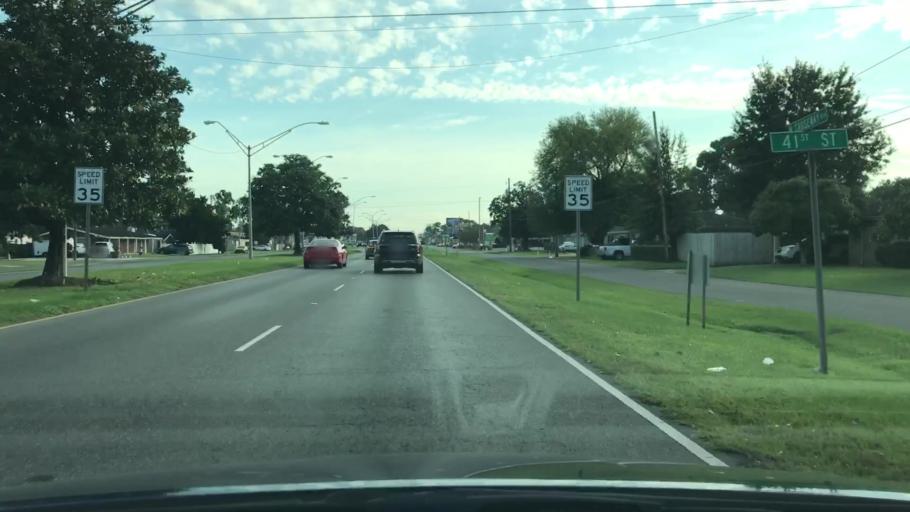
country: US
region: Louisiana
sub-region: Jefferson Parish
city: Metairie
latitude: 29.9893
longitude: -90.1559
